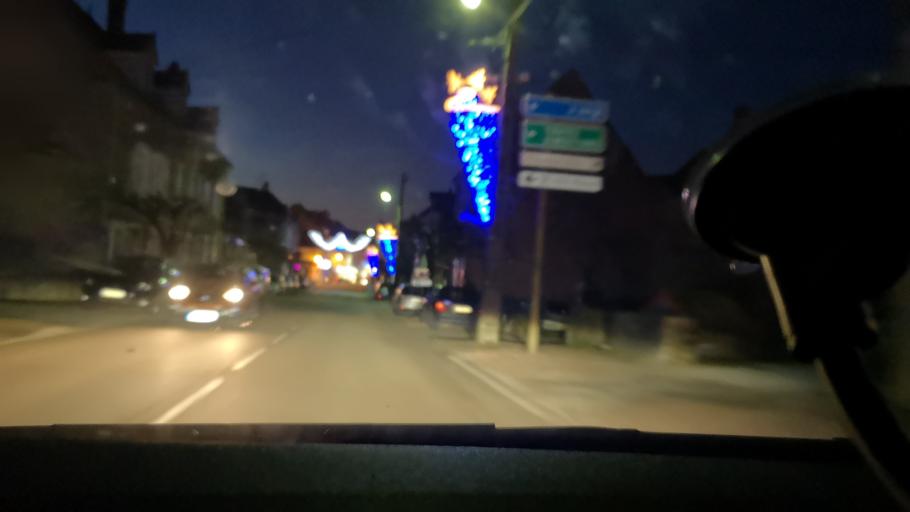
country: FR
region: Franche-Comte
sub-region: Departement du Jura
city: Poligny
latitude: 46.8332
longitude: 5.7105
